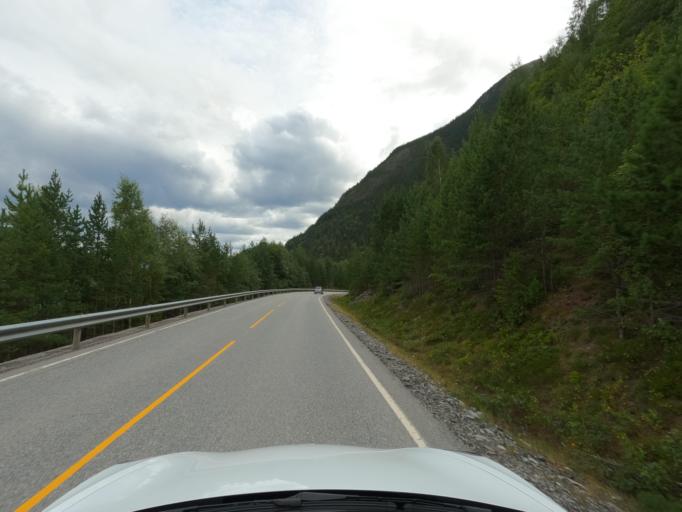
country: NO
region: Telemark
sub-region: Hjartdal
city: Sauland
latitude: 59.9053
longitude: 8.8886
